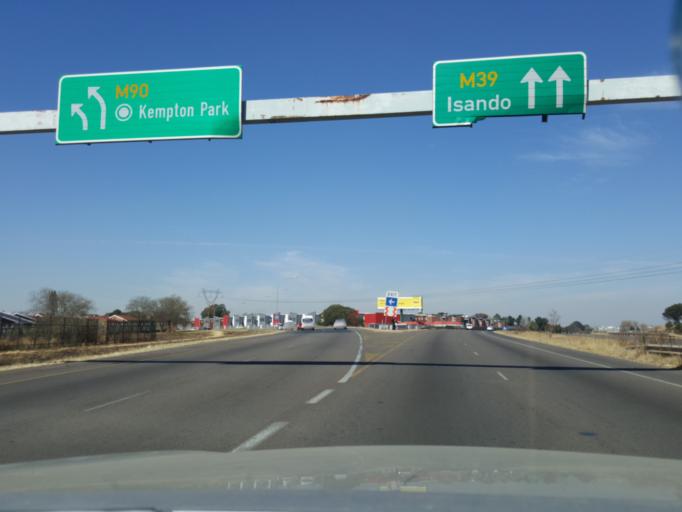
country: ZA
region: Gauteng
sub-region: City of Johannesburg Metropolitan Municipality
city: Modderfontein
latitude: -26.0918
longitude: 28.1924
